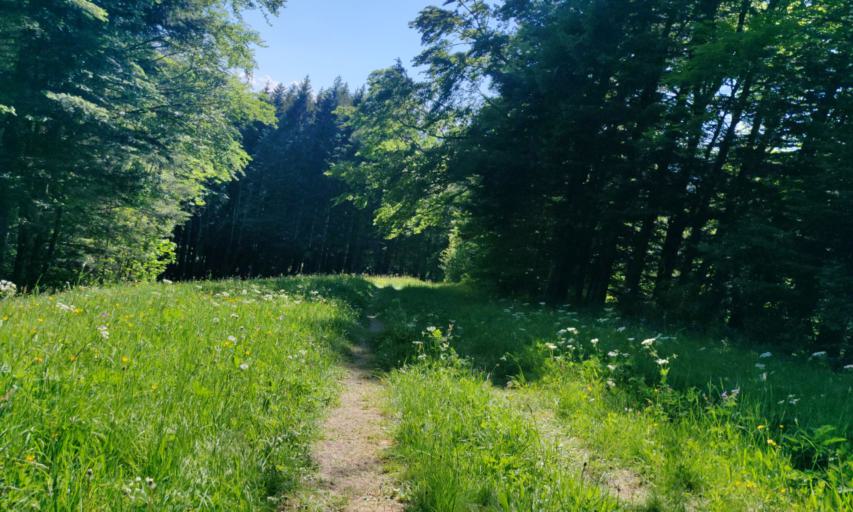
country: CH
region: Schwyz
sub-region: Bezirk Schwyz
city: Goldau
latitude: 47.0170
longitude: 8.5482
